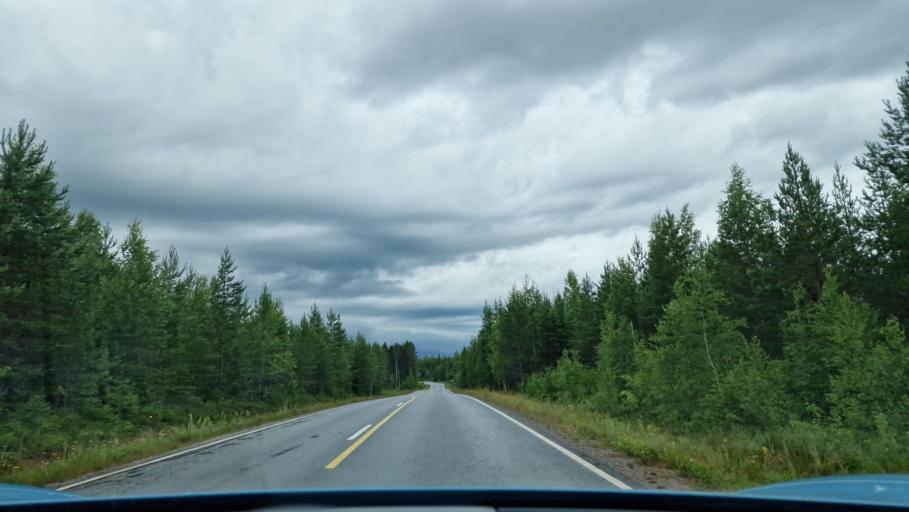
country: FI
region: Southern Ostrobothnia
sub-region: Jaerviseutu
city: Soini
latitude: 62.7140
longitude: 24.4391
